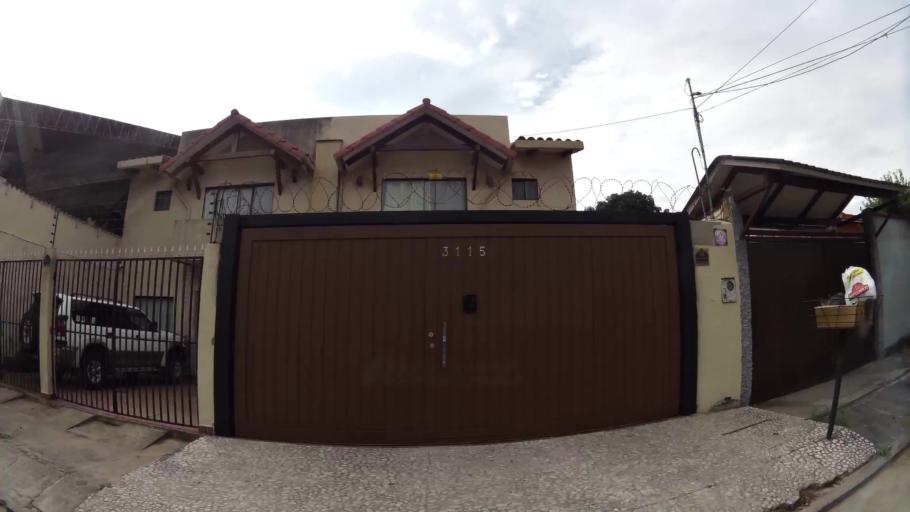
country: BO
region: Santa Cruz
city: Santa Cruz de la Sierra
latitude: -17.7809
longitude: -63.2145
